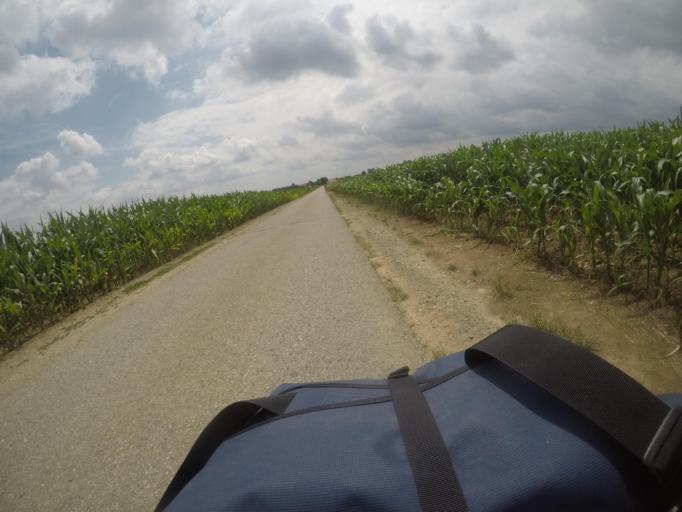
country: DE
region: Bavaria
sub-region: Swabia
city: Fellheim
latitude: 48.0808
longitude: 10.1560
